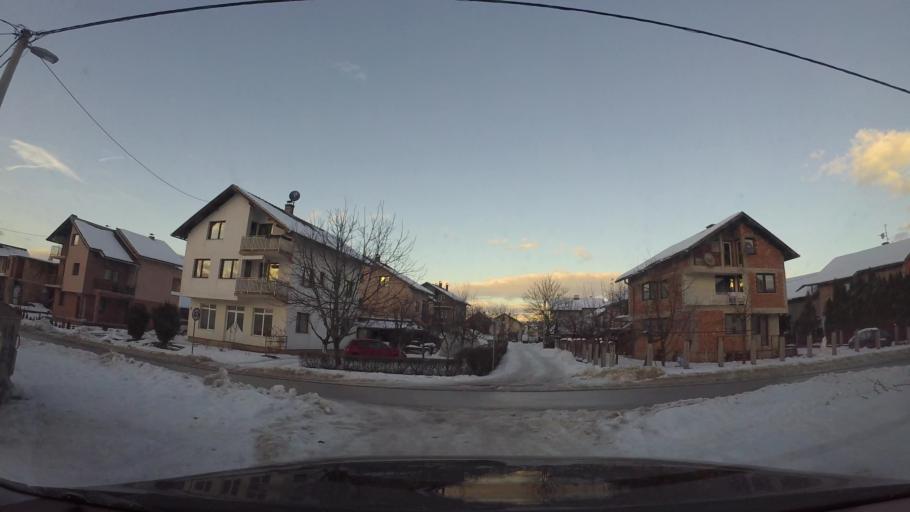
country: BA
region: Federation of Bosnia and Herzegovina
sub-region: Kanton Sarajevo
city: Sarajevo
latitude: 43.8082
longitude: 18.3672
